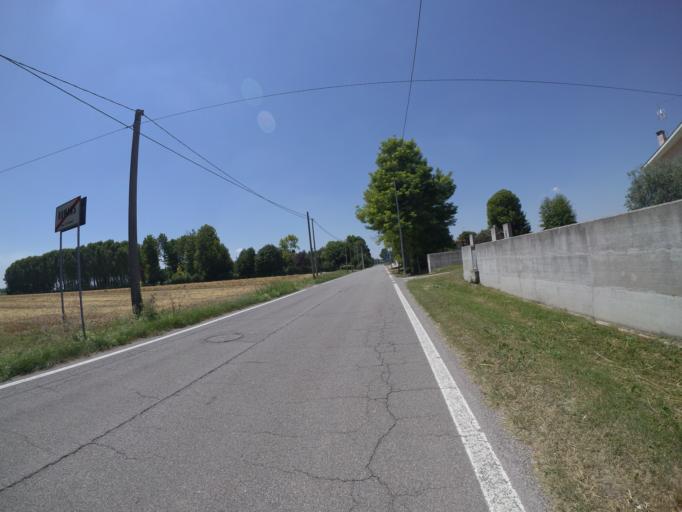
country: IT
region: Friuli Venezia Giulia
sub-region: Provincia di Udine
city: Varmo
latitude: 45.8972
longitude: 13.0142
